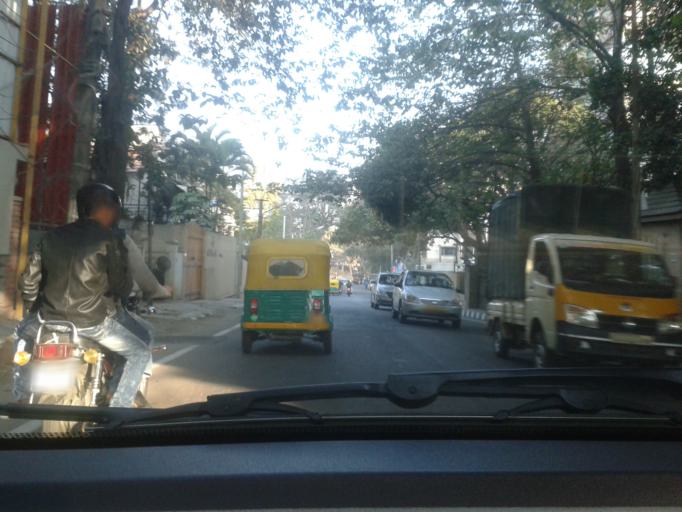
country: IN
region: Karnataka
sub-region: Bangalore Urban
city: Bangalore
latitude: 12.9985
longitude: 77.6005
